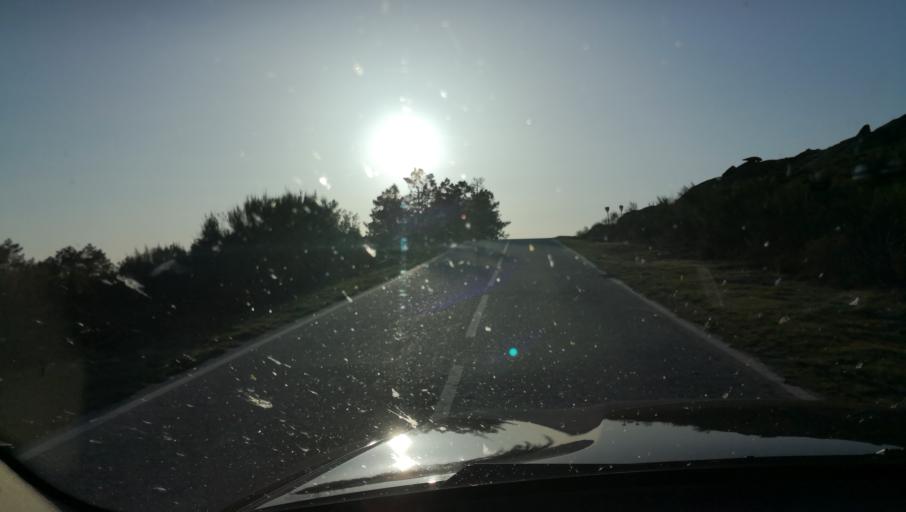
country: PT
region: Vila Real
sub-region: Vila Real
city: Vila Real
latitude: 41.3801
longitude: -7.8170
